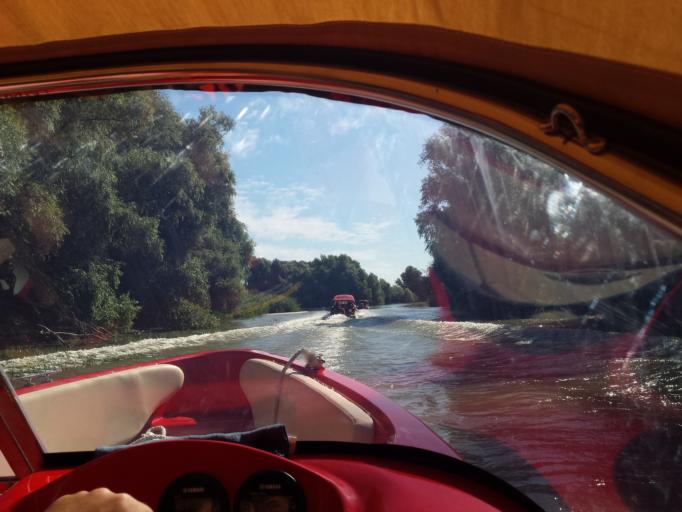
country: RO
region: Tulcea
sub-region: Comuna Pardina
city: Pardina
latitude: 45.2470
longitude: 29.0569
